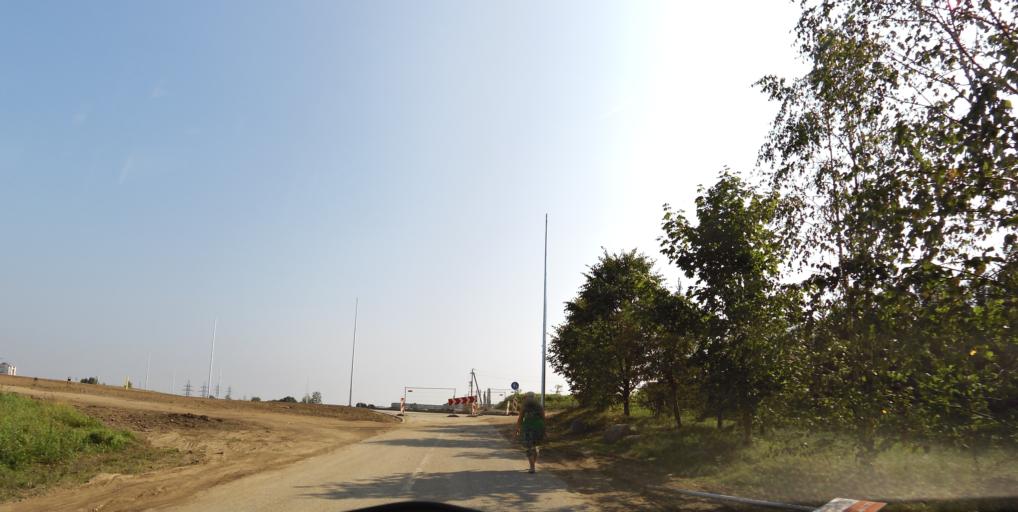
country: LT
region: Vilnius County
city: Justiniskes
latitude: 54.7248
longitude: 25.2050
